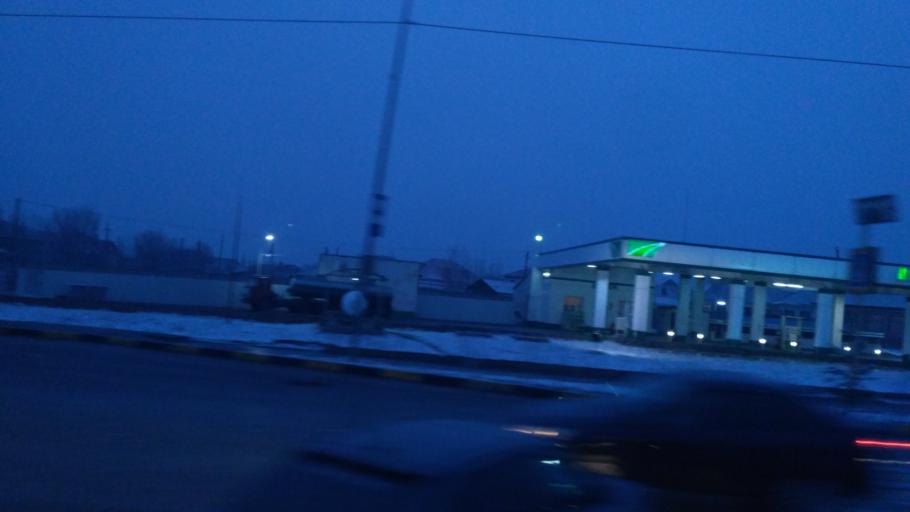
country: KZ
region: Ongtustik Qazaqstan
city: Shymkent
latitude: 42.3445
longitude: 69.5405
